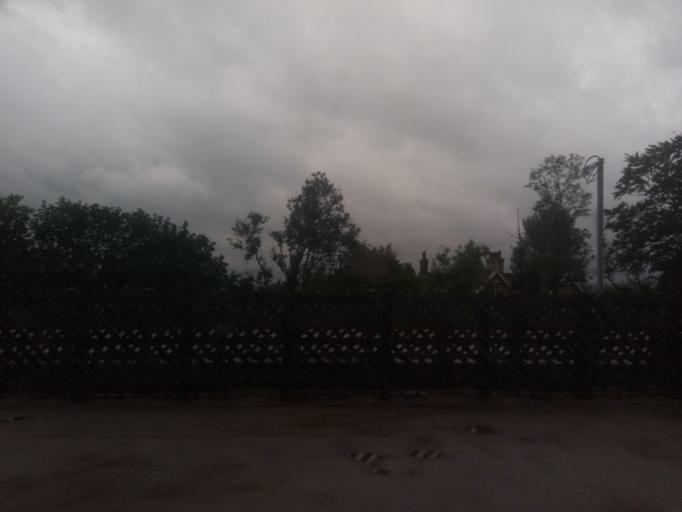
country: GB
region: England
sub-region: North Yorkshire
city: Settle
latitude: 54.0107
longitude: -2.2271
